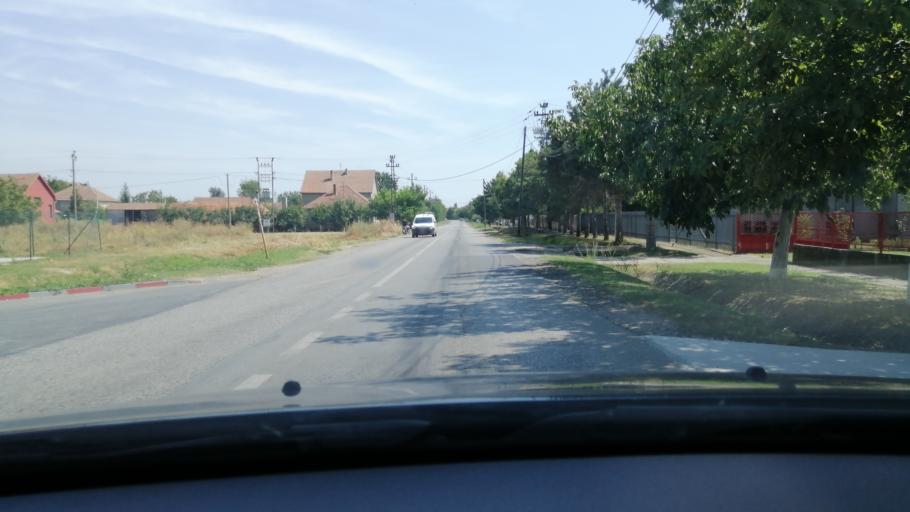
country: RS
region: Autonomna Pokrajina Vojvodina
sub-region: Srednjebanatski Okrug
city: Secanj
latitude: 45.3685
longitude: 20.7614
